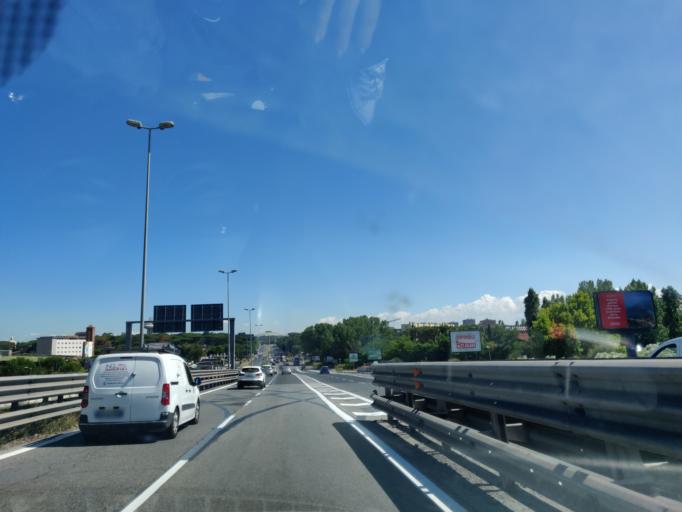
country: IT
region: Latium
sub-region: Citta metropolitana di Roma Capitale
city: Selcetta
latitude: 41.8141
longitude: 12.4607
